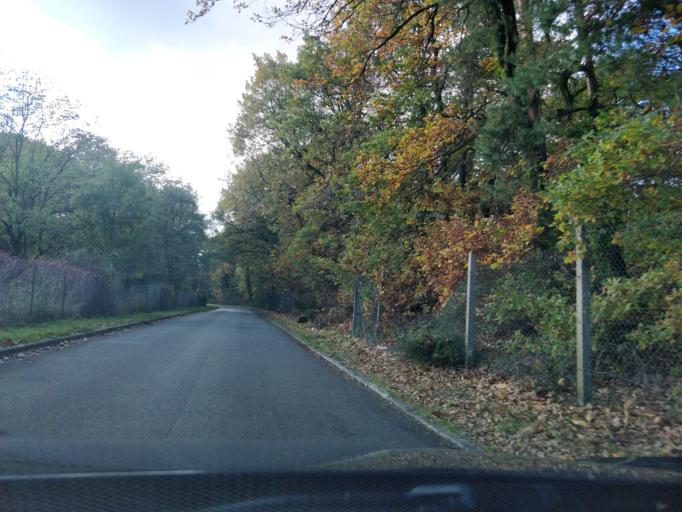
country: FR
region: Ile-de-France
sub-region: Departement de l'Essonne
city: Briis-sous-Forges
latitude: 48.6271
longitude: 2.1321
